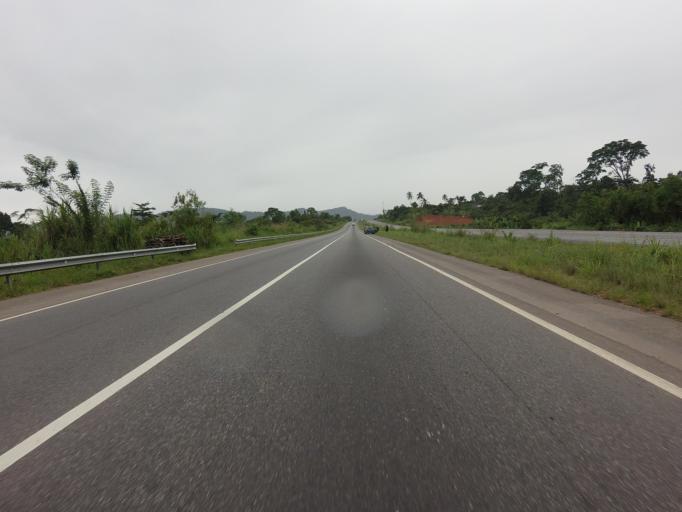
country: GH
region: Eastern
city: Suhum
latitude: 6.1037
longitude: -0.4853
